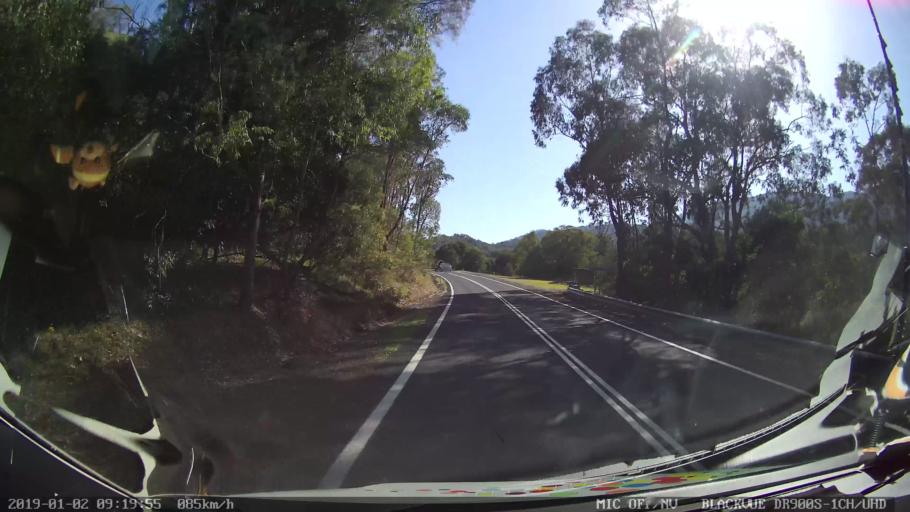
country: AU
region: New South Wales
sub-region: Tumut Shire
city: Tumut
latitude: -35.4171
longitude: 148.2789
